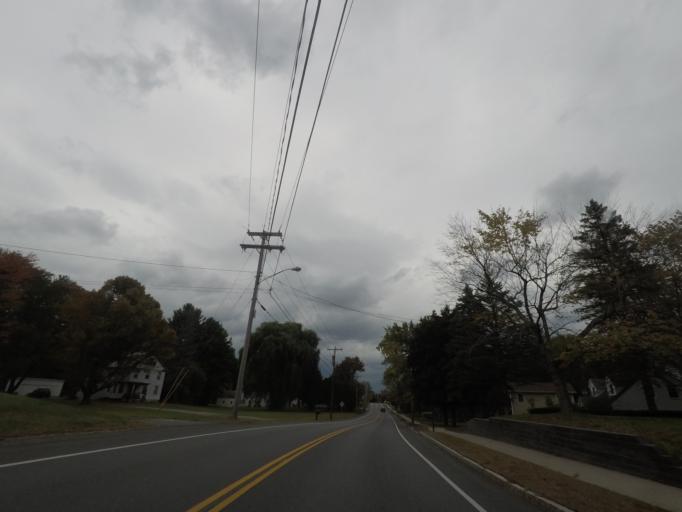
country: US
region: New York
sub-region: Albany County
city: McKownville
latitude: 42.6661
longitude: -73.8479
